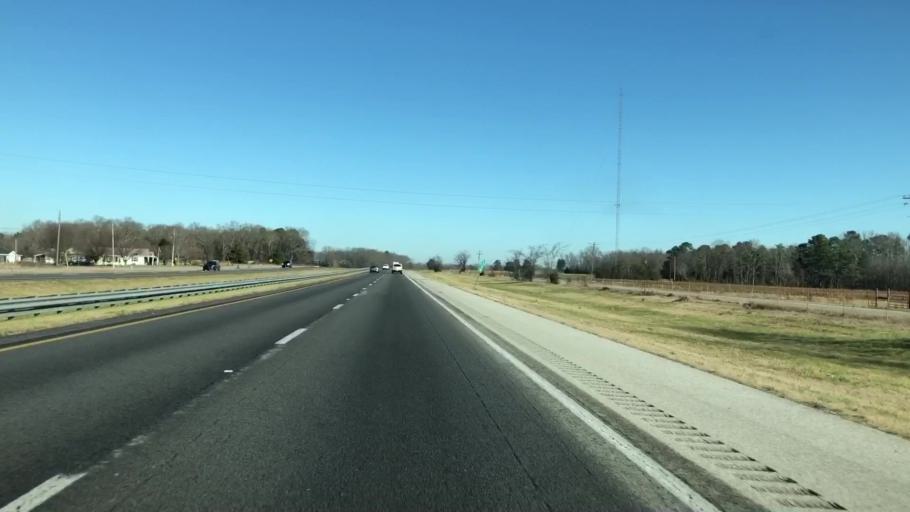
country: US
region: Alabama
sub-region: Limestone County
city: Athens
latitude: 34.8810
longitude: -86.9192
